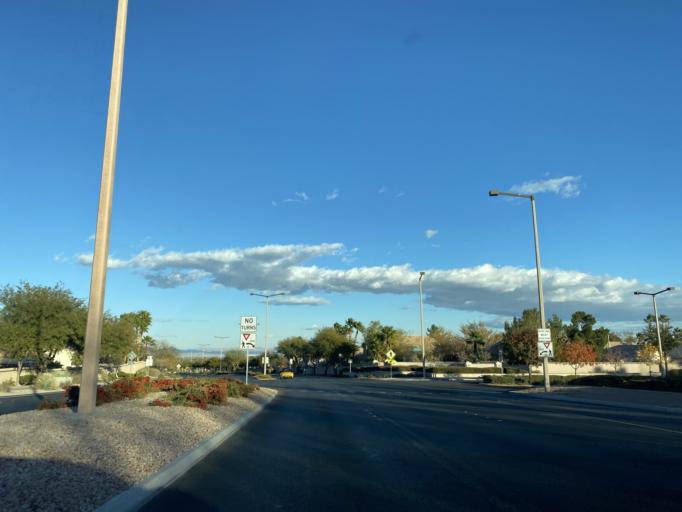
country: US
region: Nevada
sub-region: Clark County
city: Summerlin South
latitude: 36.2043
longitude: -115.3094
